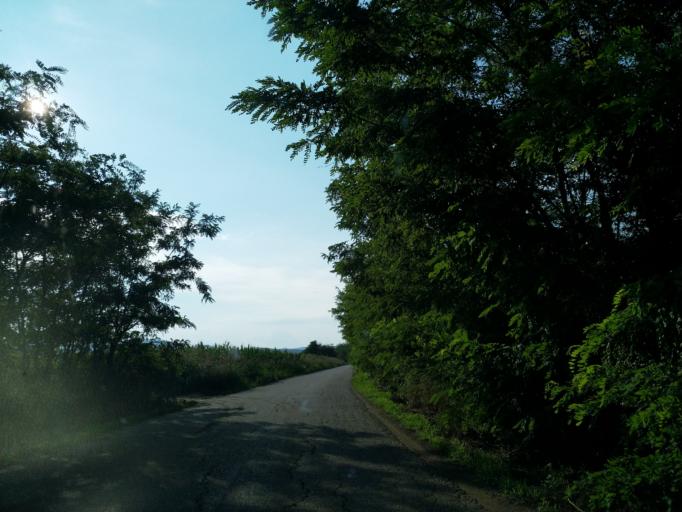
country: RS
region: Central Serbia
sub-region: Pomoravski Okrug
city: Jagodina
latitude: 43.9897
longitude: 21.2086
